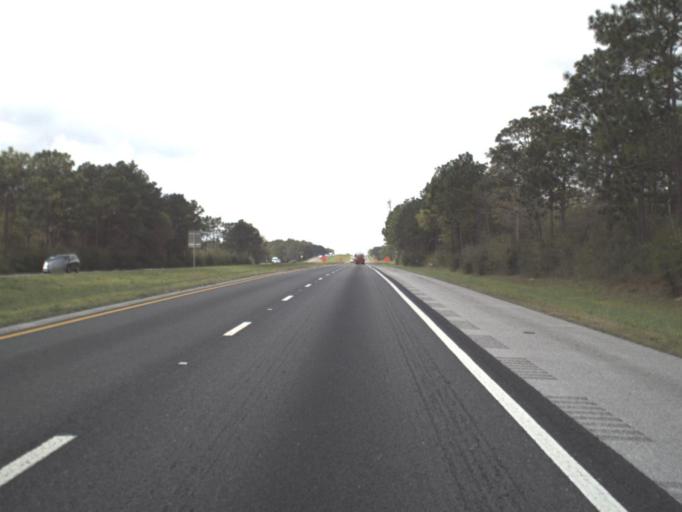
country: US
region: Florida
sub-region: Okaloosa County
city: Crestview
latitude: 30.7022
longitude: -86.7426
